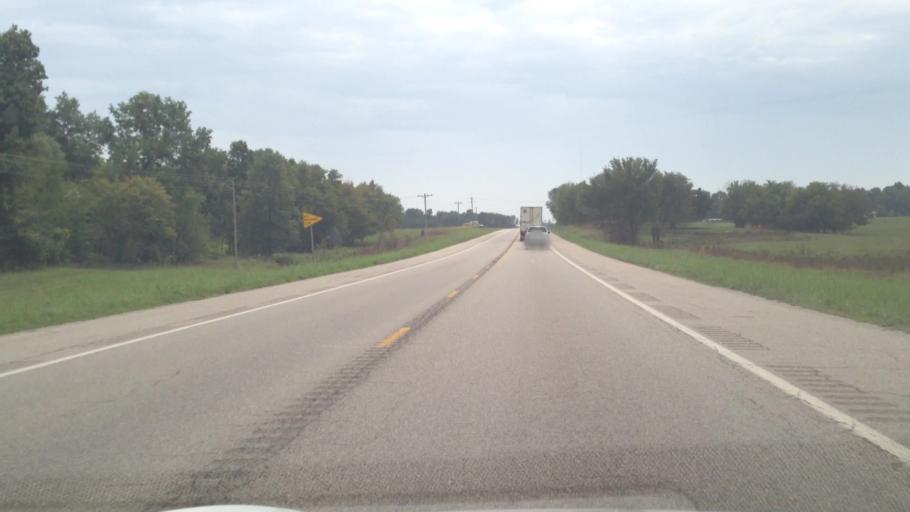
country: US
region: Kansas
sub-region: Crawford County
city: Pittsburg
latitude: 37.2547
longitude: -94.7052
